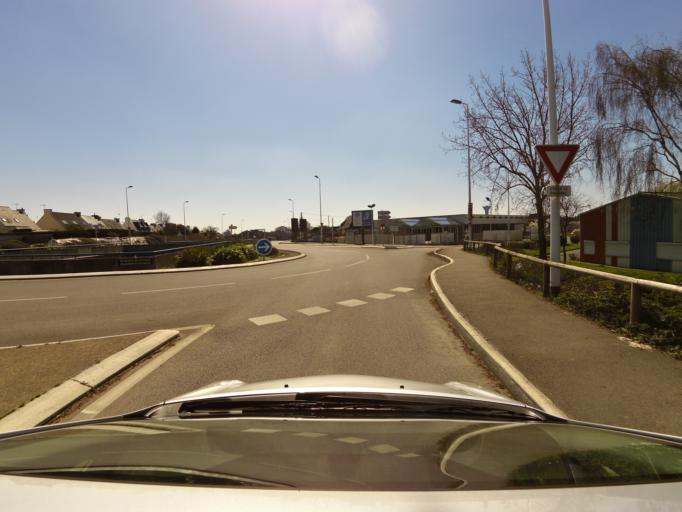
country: FR
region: Brittany
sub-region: Departement du Morbihan
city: Larmor-Plage
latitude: 47.7269
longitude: -3.3840
